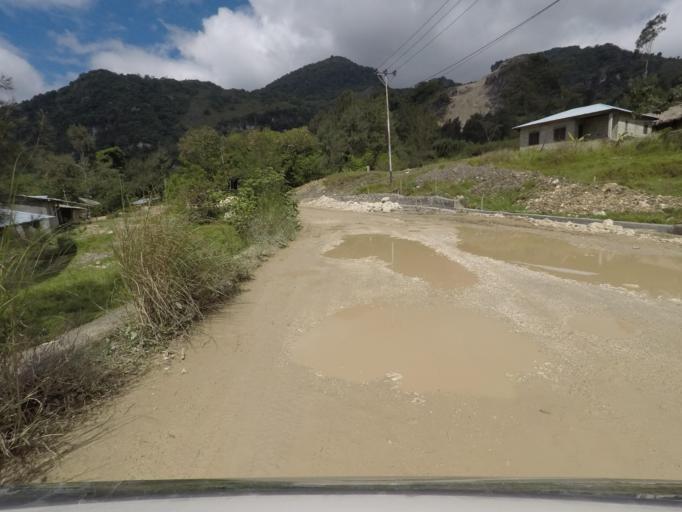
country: TL
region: Baucau
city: Venilale
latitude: -8.7093
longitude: 126.3641
